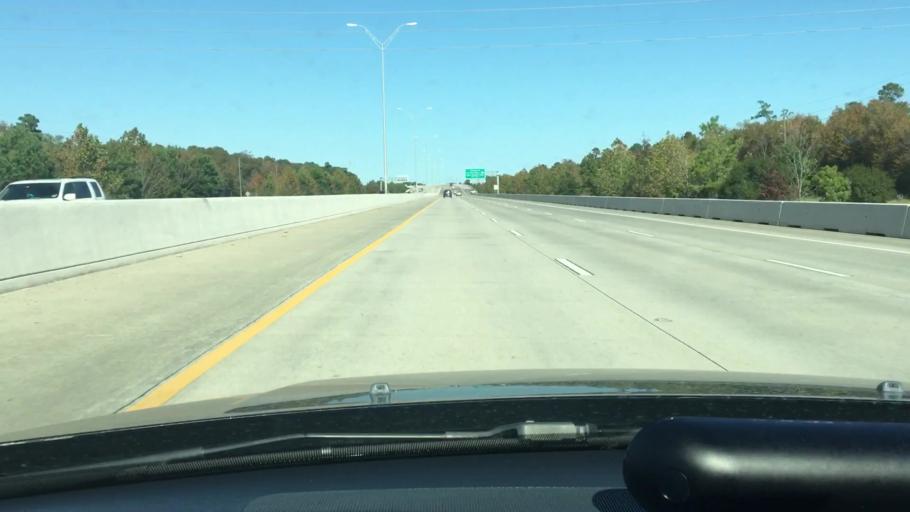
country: US
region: Texas
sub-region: Harris County
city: Sheldon
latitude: 29.8629
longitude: -95.1871
